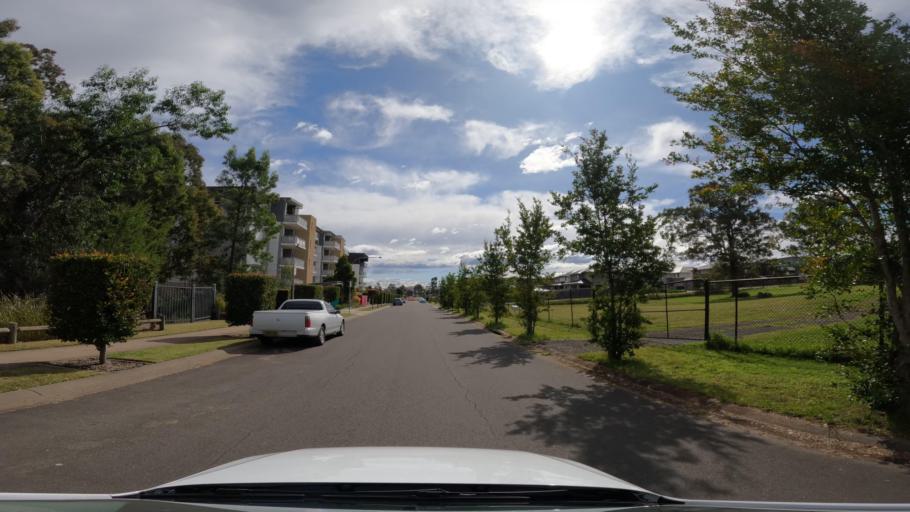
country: AU
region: New South Wales
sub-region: Blacktown
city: Stanhope Gardens
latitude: -33.7208
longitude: 150.9449
